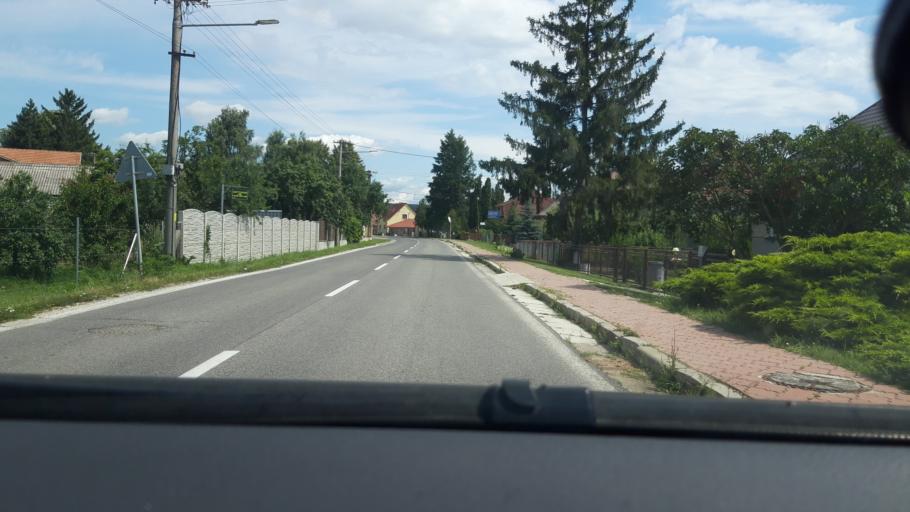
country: SK
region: Trenciansky
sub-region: Okres Nove Mesto nad Vahom
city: Nove Mesto nad Vahom
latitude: 48.7438
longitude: 17.8868
